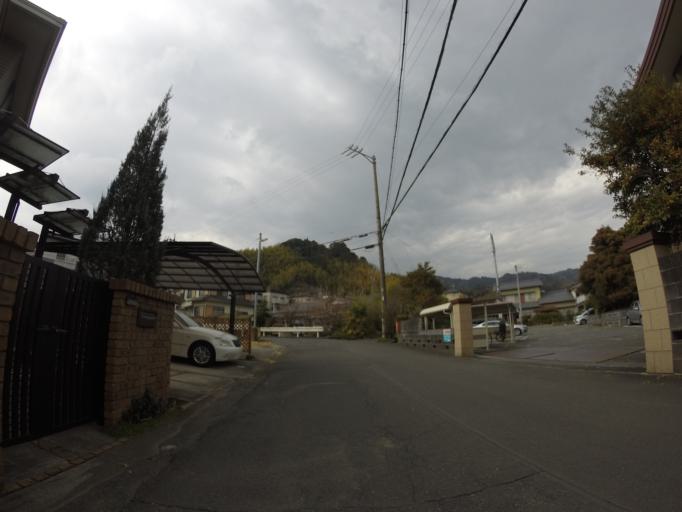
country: JP
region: Shizuoka
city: Shizuoka-shi
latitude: 35.0418
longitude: 138.4634
